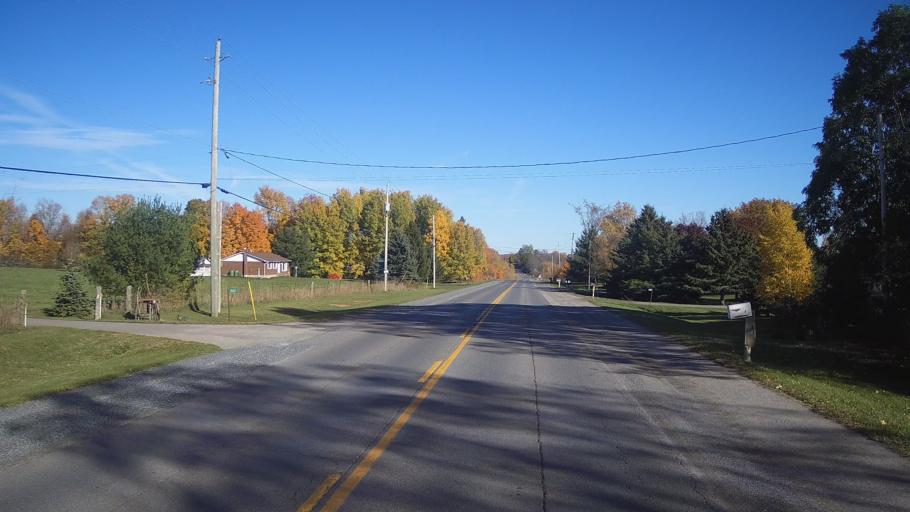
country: CA
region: Ontario
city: Kingston
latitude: 44.4071
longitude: -76.5449
